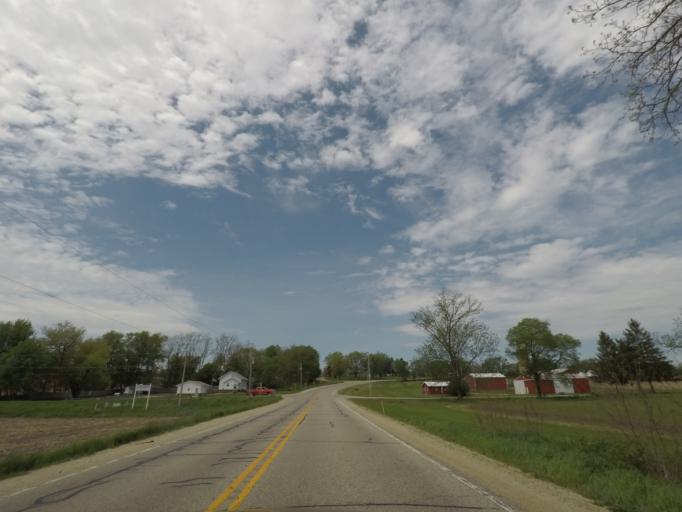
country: US
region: Wisconsin
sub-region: Rock County
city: Orfordville
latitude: 42.5995
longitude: -89.2075
